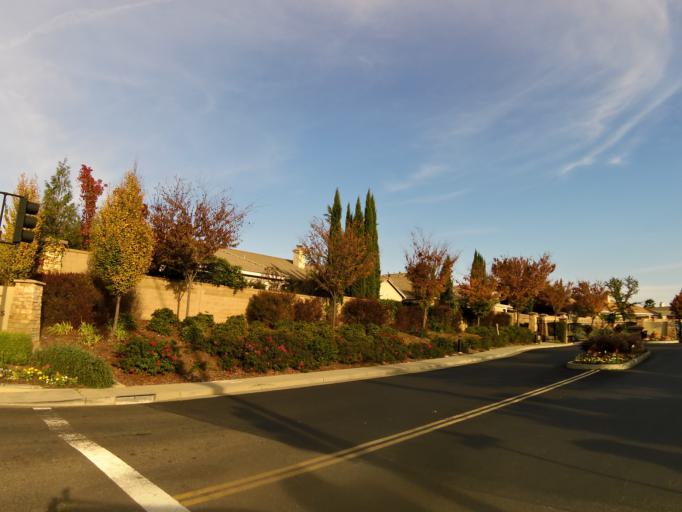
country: US
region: California
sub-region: El Dorado County
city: El Dorado Hills
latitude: 38.6371
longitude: -121.0766
